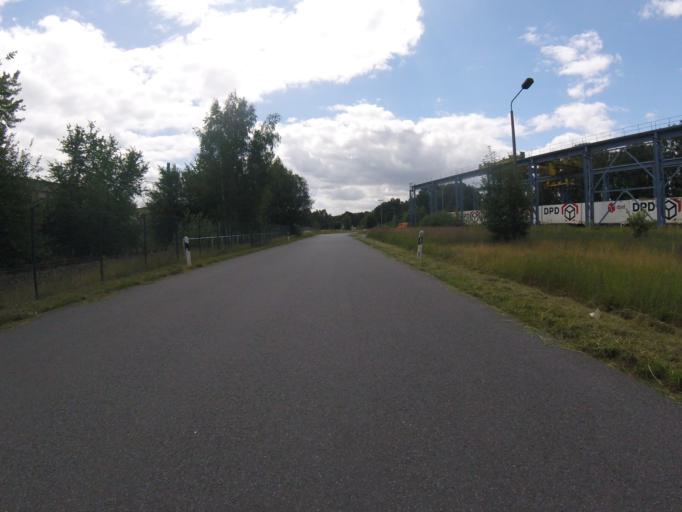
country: DE
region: Brandenburg
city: Mittenwalde
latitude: 52.2470
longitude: 13.5183
